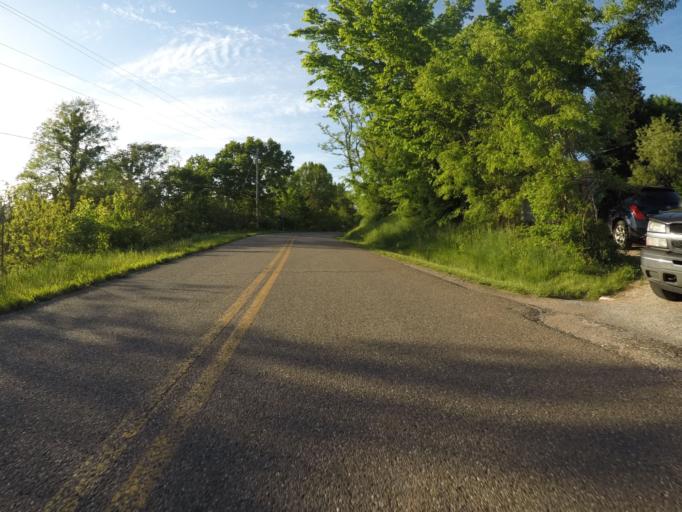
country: US
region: West Virginia
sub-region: Cabell County
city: Huntington
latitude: 38.5377
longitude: -82.4244
